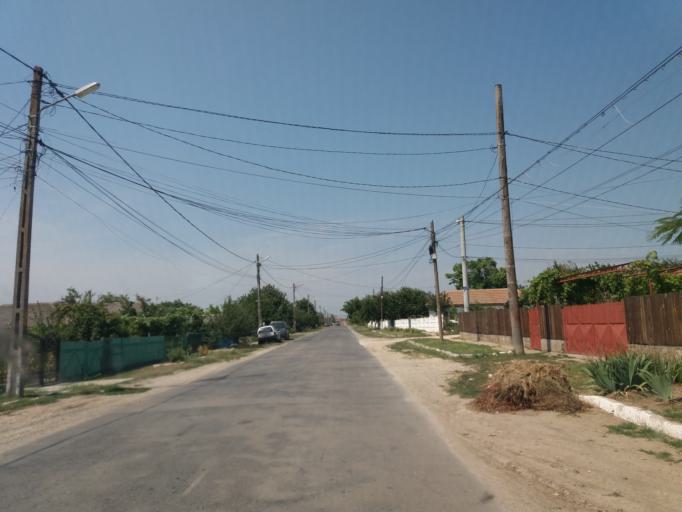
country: RO
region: Constanta
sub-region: Comuna Corbu
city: Corbu
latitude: 44.3993
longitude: 28.6617
